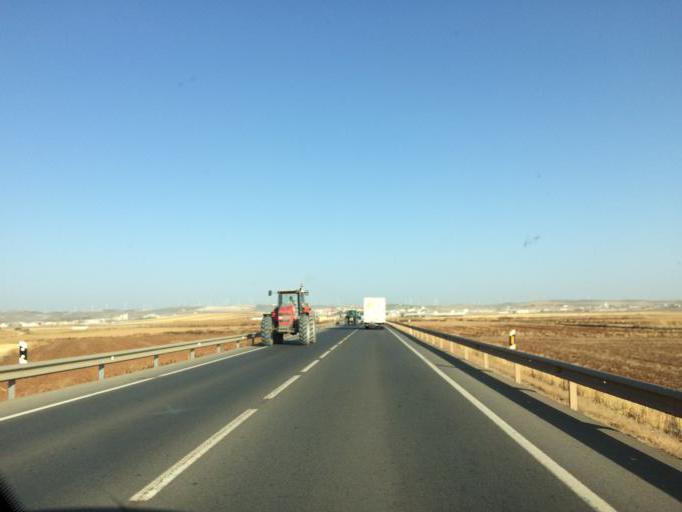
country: ES
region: Andalusia
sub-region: Provincia de Malaga
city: Campillos
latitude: 37.0480
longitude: -4.8385
